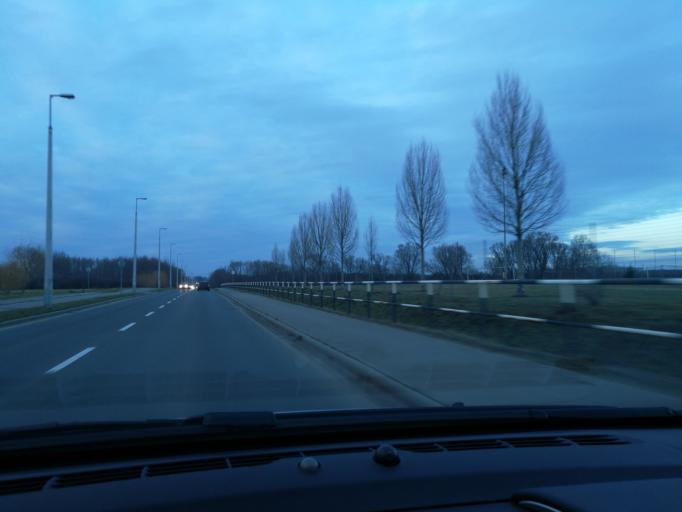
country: HU
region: Szabolcs-Szatmar-Bereg
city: Nyiregyhaza
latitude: 47.9628
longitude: 21.7438
